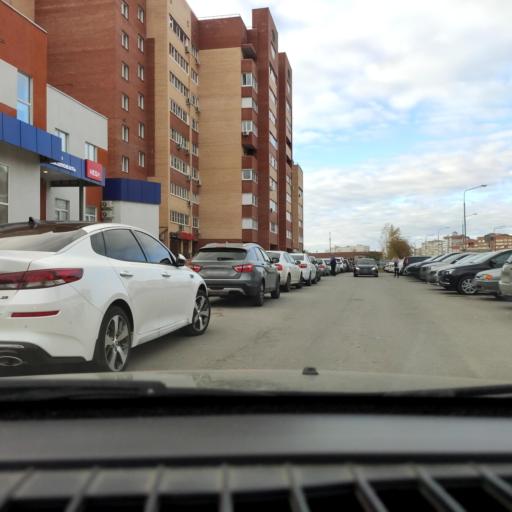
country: RU
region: Samara
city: Tol'yatti
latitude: 53.5363
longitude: 49.3539
